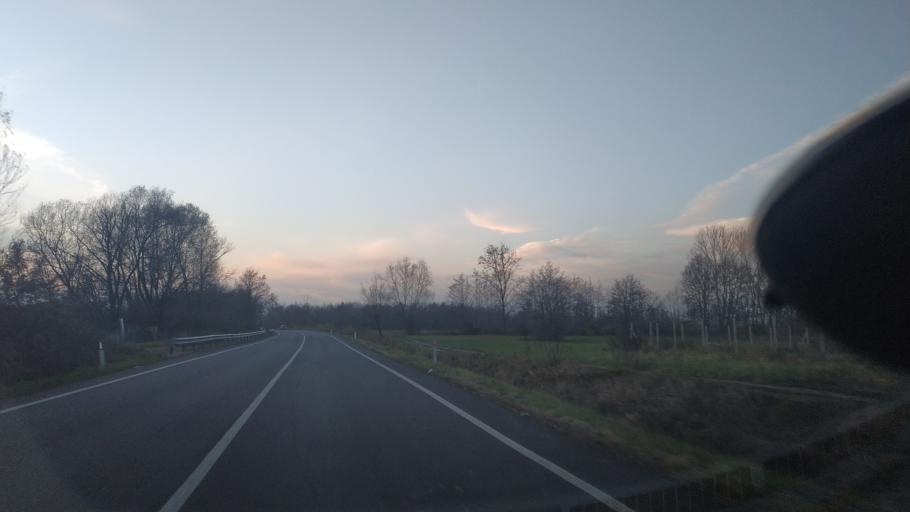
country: IT
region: Piedmont
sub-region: Provincia di Torino
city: Montanaro
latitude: 45.2429
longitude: 7.8551
